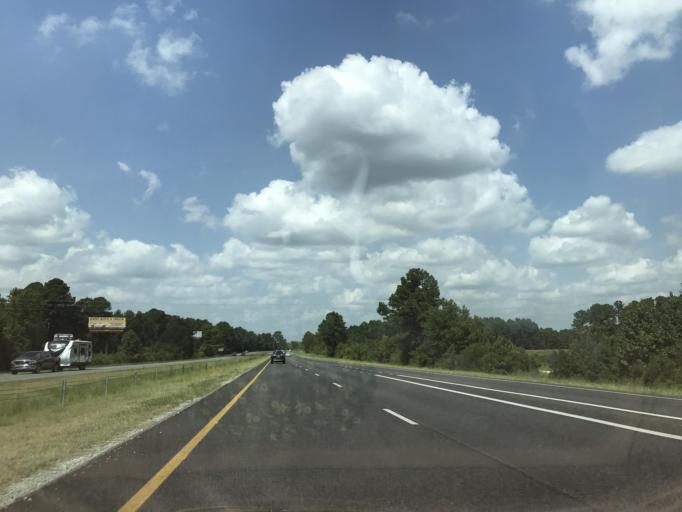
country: US
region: North Carolina
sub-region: Duplin County
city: Wallace
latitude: 34.7724
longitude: -77.9677
